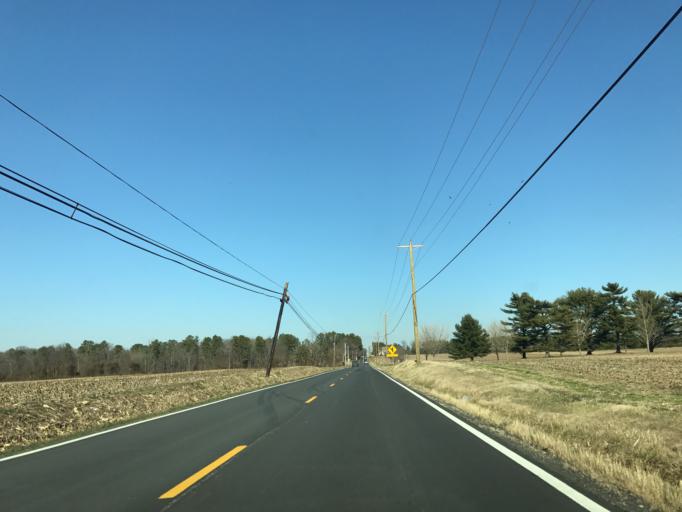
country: US
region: Maryland
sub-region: Queen Anne's County
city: Grasonville
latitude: 38.9965
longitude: -76.1408
